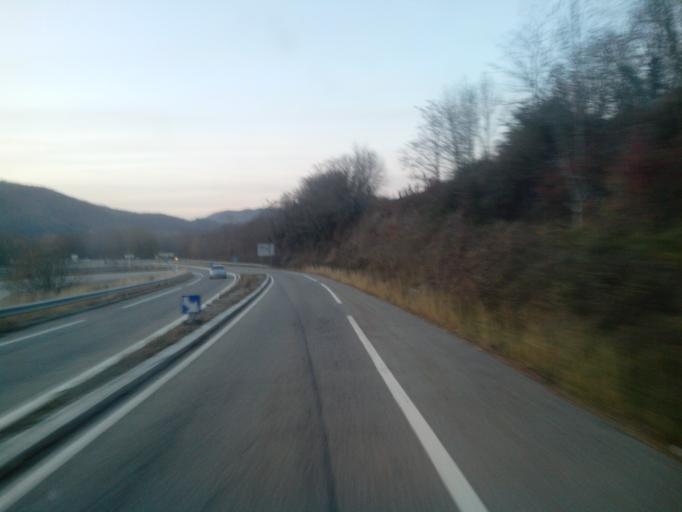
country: FR
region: Midi-Pyrenees
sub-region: Departement de l'Ariege
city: Montgaillard
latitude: 42.9204
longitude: 1.6391
